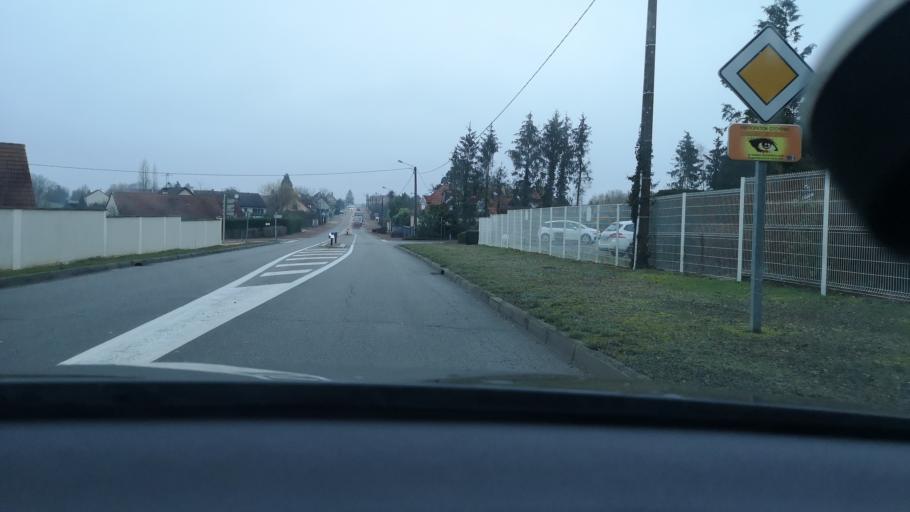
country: FR
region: Bourgogne
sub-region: Departement de la Cote-d'Or
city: Fenay
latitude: 47.1658
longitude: 5.0830
